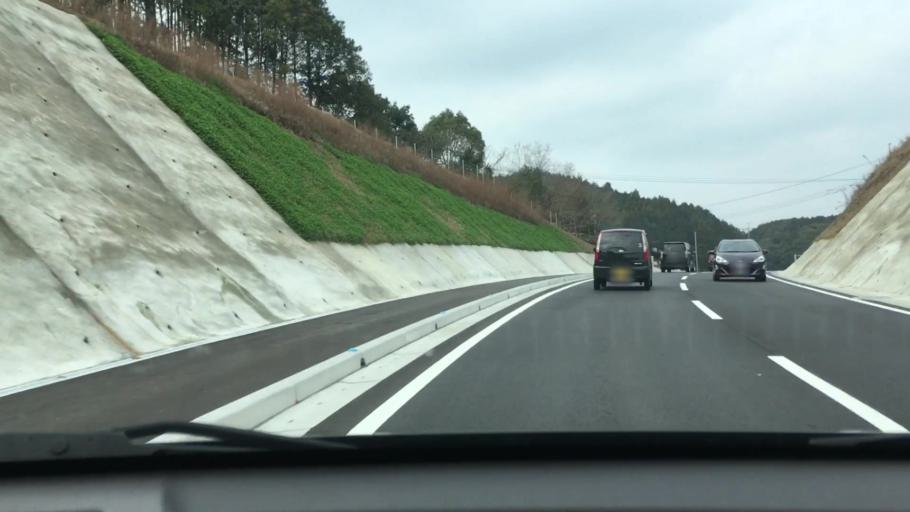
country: JP
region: Saga Prefecture
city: Imaricho-ko
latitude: 33.3402
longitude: 129.9218
